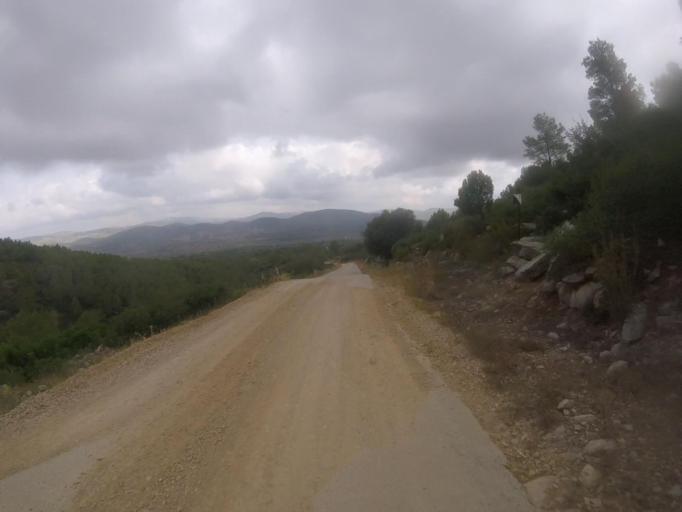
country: ES
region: Valencia
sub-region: Provincia de Castello
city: Santa Magdalena de Pulpis
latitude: 40.3315
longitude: 0.2796
